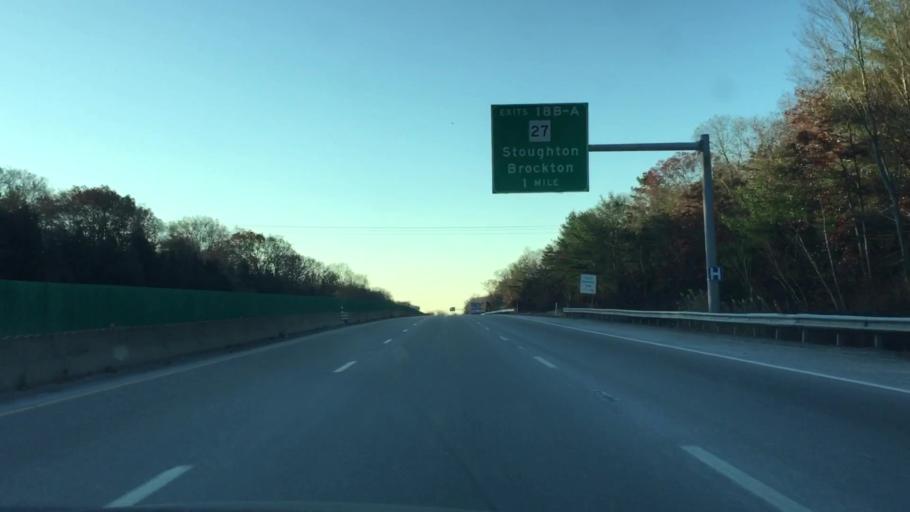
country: US
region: Massachusetts
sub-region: Norfolk County
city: Avon
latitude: 42.1120
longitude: -71.0596
